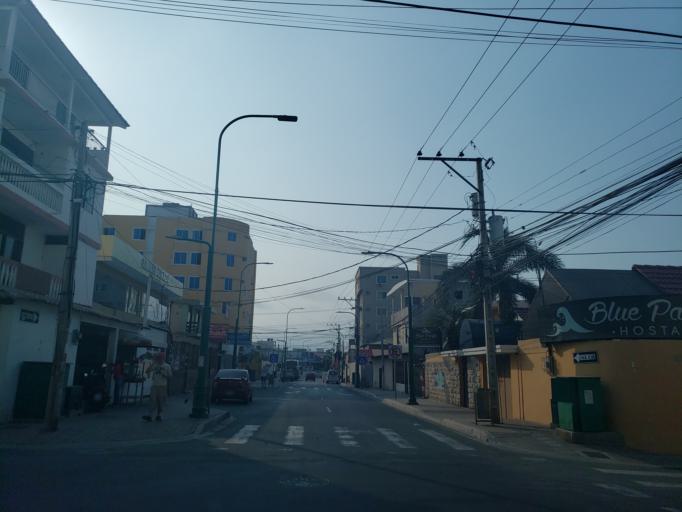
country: EC
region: Manabi
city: Manta
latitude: -0.9446
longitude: -80.7394
